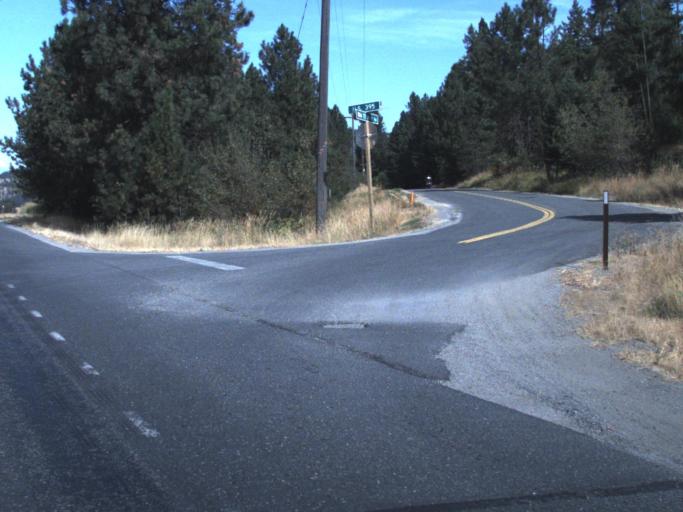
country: US
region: Washington
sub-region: Stevens County
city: Colville
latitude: 48.3998
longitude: -117.8496
